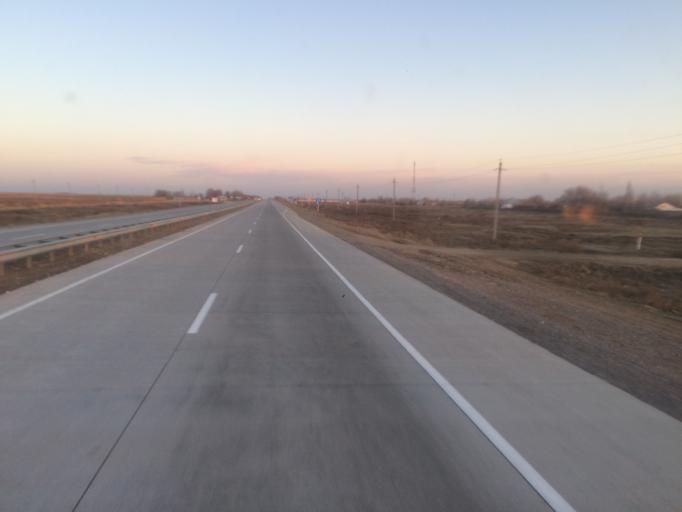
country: KZ
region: Ongtustik Qazaqstan
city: Bayaldyr
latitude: 43.0646
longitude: 68.6768
